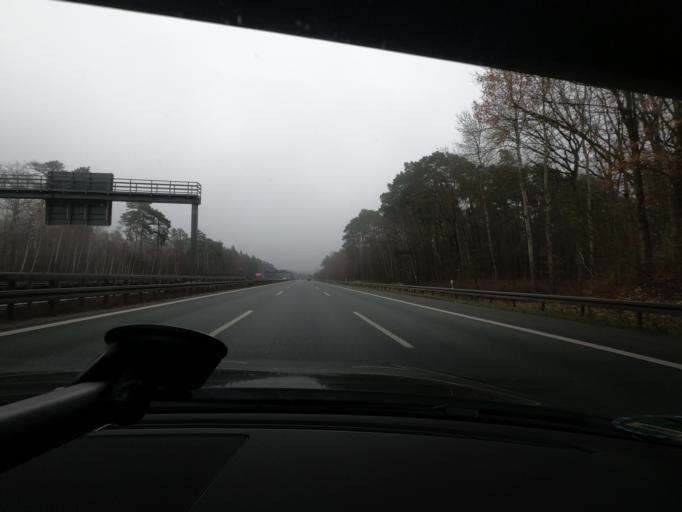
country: DE
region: Bavaria
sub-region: Regierungsbezirk Mittelfranken
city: Buckenhof
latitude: 49.5324
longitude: 11.0509
